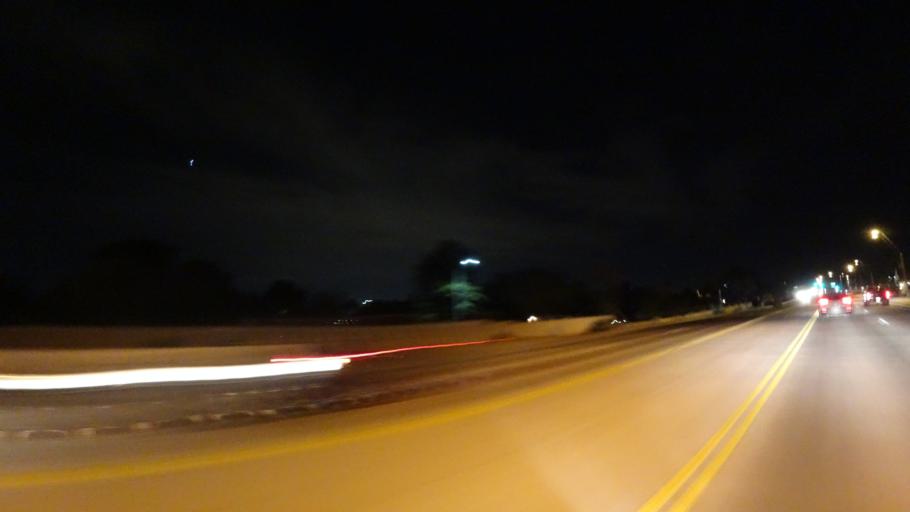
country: US
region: Arizona
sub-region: Maricopa County
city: Gilbert
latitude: 33.3617
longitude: -111.7732
